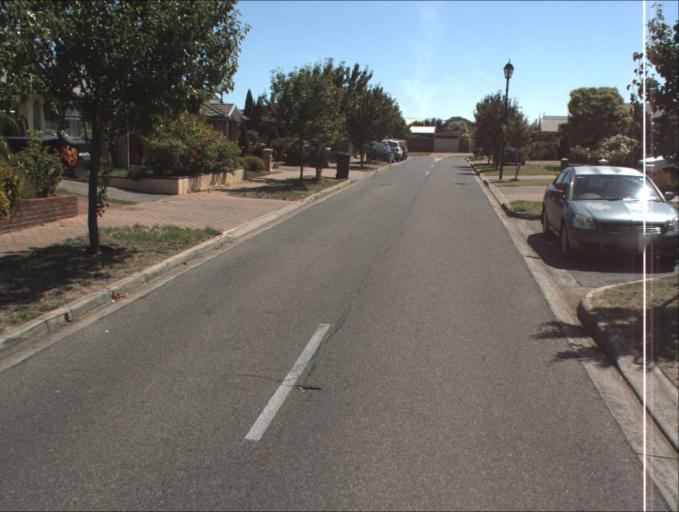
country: AU
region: South Australia
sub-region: Port Adelaide Enfield
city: Gilles Plains
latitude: -34.8557
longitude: 138.6417
